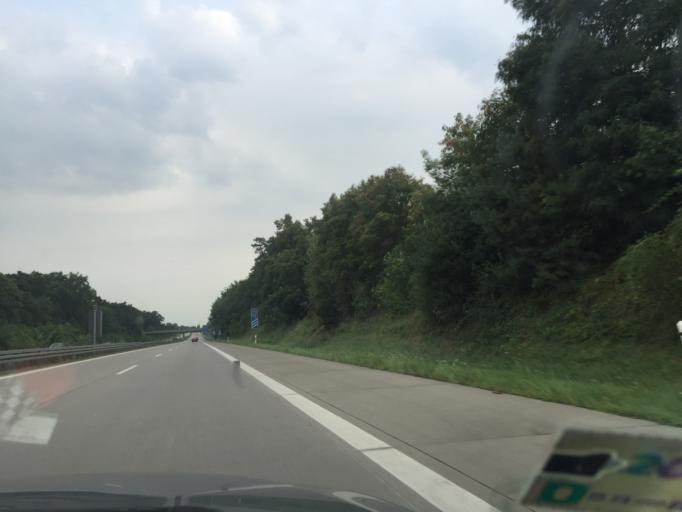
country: DE
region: Brandenburg
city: Bernau bei Berlin
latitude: 52.6956
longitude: 13.5557
